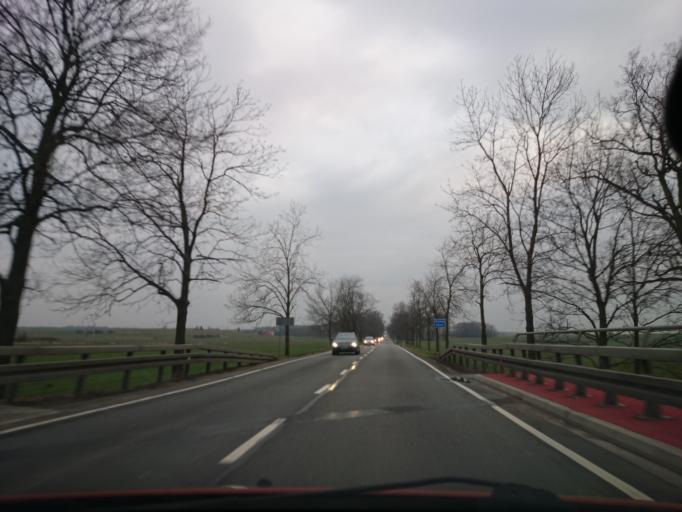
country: PL
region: Opole Voivodeship
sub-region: Powiat nyski
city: Pakoslawice
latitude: 50.5256
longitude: 17.3594
